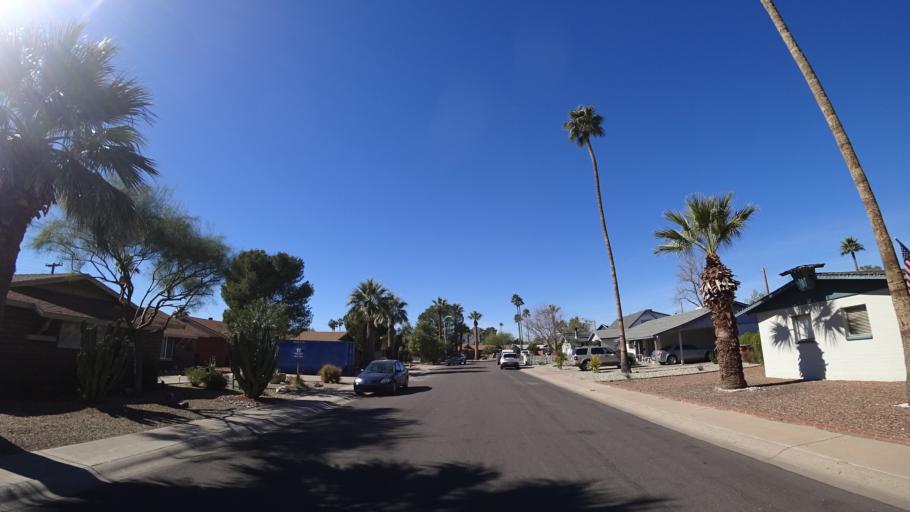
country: US
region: Arizona
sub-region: Maricopa County
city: Scottsdale
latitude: 33.5145
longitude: -111.8966
